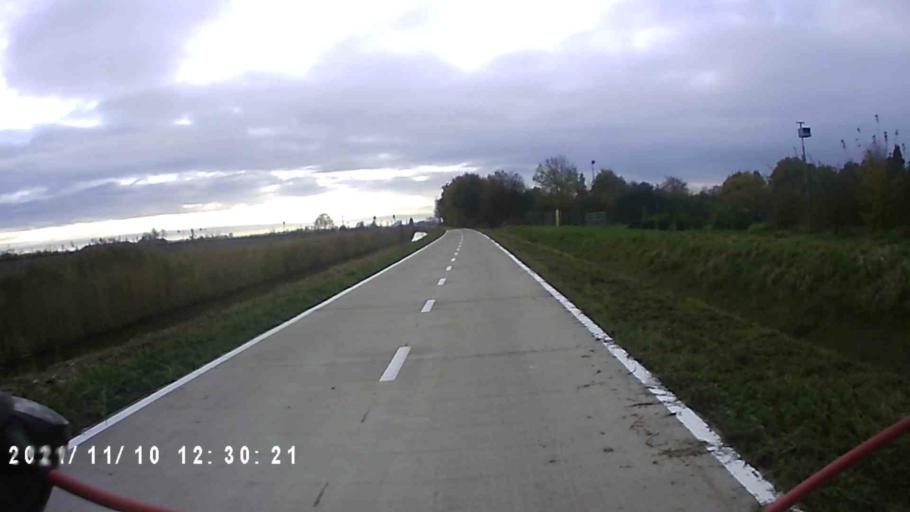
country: NL
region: Groningen
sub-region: Gemeente Groningen
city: Korrewegwijk
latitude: 53.2774
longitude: 6.5397
